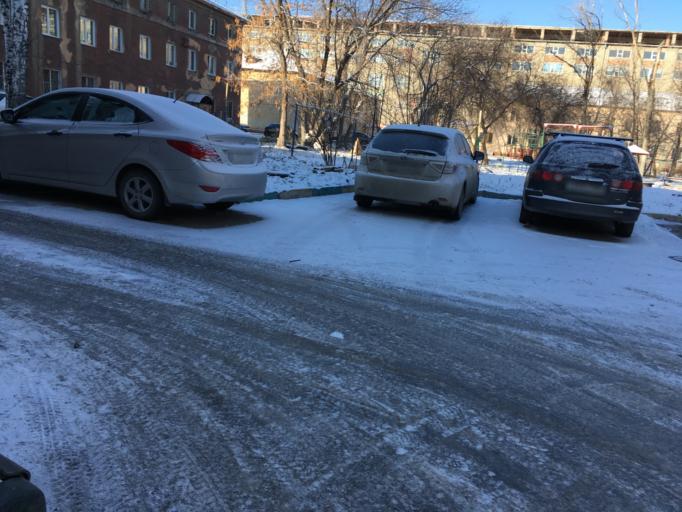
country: RU
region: Novosibirsk
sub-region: Novosibirskiy Rayon
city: Novosibirsk
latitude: 55.0548
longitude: 82.9655
